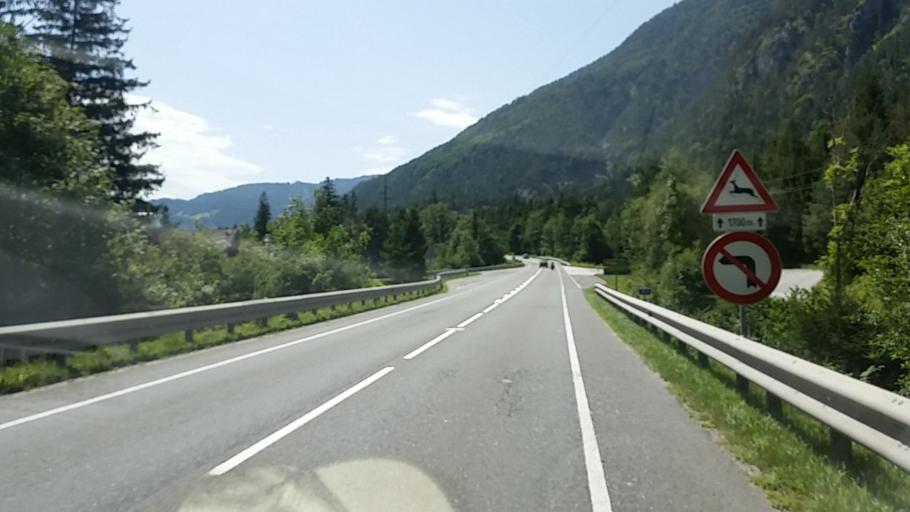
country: AT
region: Salzburg
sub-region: Politischer Bezirk Sankt Johann im Pongau
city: Werfen
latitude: 47.5199
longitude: 13.1654
